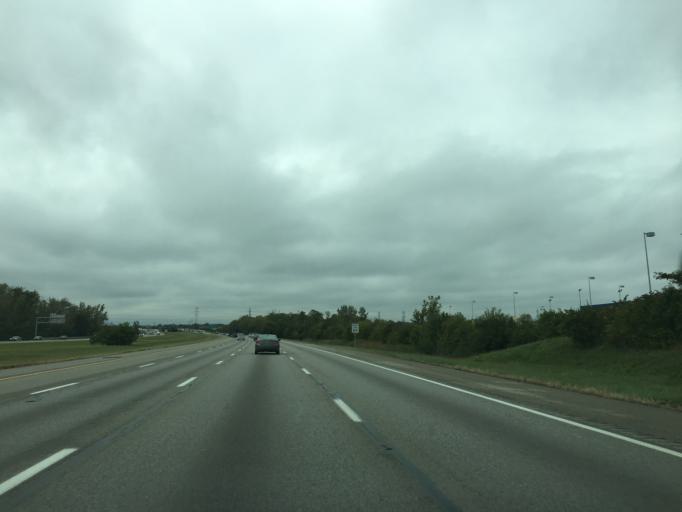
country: US
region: Ohio
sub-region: Butler County
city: Beckett Ridge
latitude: 39.3155
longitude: -84.4315
